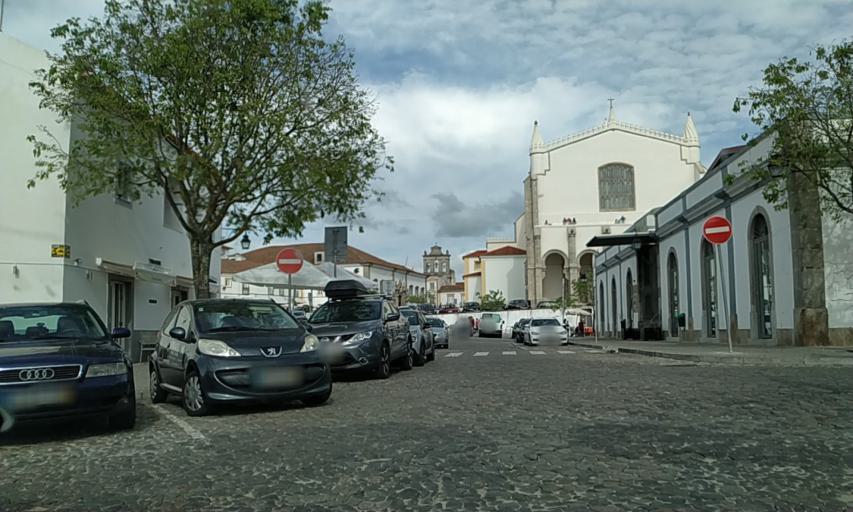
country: PT
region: Evora
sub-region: Evora
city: Evora
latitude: 38.5689
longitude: -7.9100
